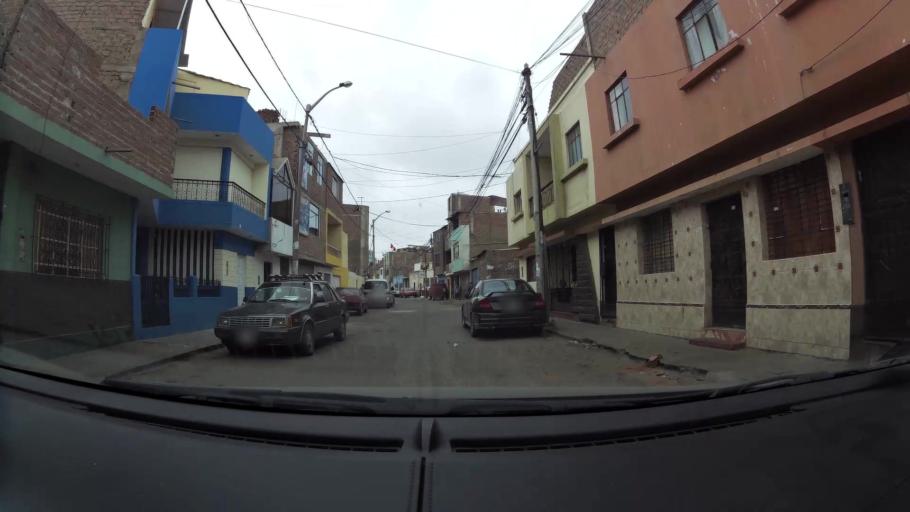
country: PE
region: La Libertad
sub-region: Provincia de Trujillo
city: Trujillo
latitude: -8.1150
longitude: -79.0169
